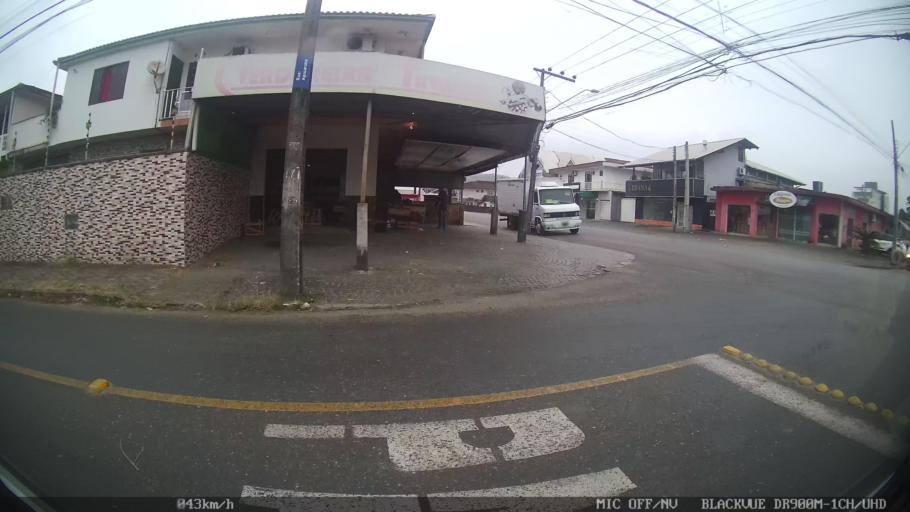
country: BR
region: Santa Catarina
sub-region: Joinville
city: Joinville
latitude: -26.2772
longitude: -48.8083
